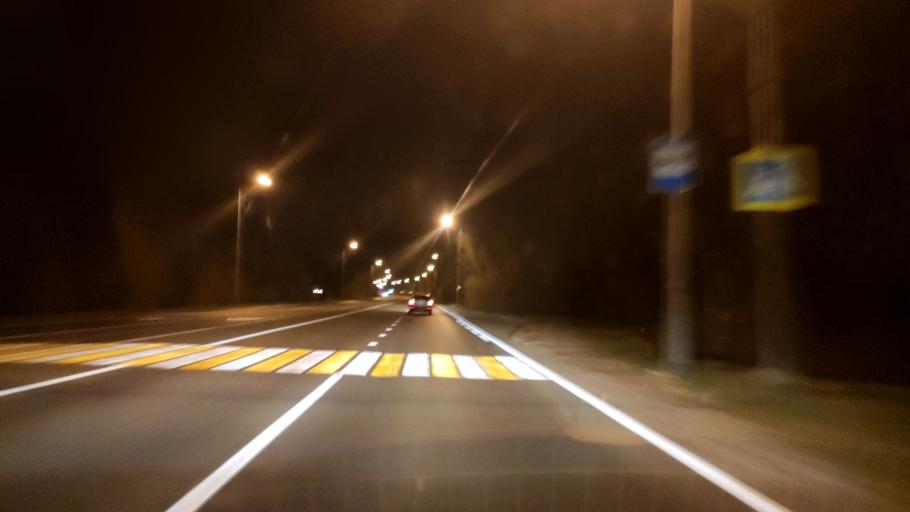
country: RU
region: Belgorod
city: Staryy Oskol
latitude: 51.3488
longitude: 37.8257
